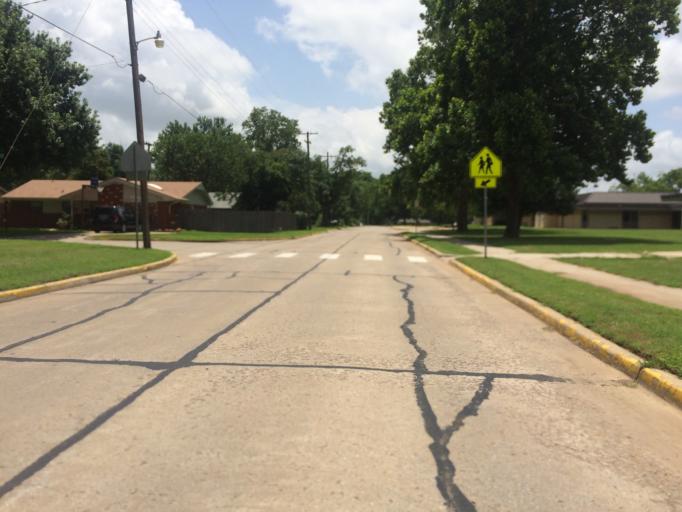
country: US
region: Oklahoma
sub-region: Cleveland County
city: Norman
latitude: 35.2133
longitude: -97.4690
